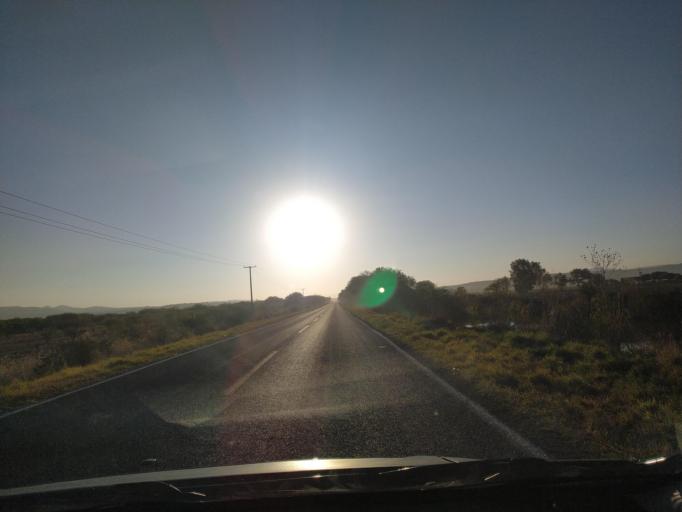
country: MX
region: Guanajuato
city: Ciudad Manuel Doblado
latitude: 20.7375
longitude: -101.8625
